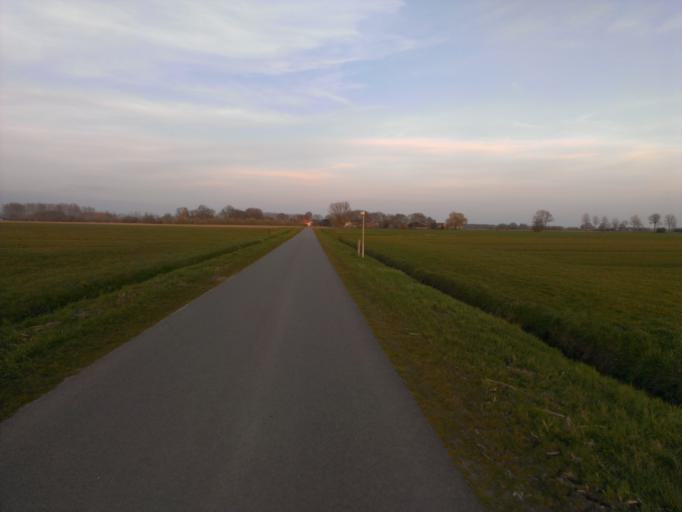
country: NL
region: Overijssel
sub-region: Gemeente Olst-Wijhe
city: Wijhe
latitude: 52.3990
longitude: 6.0958
